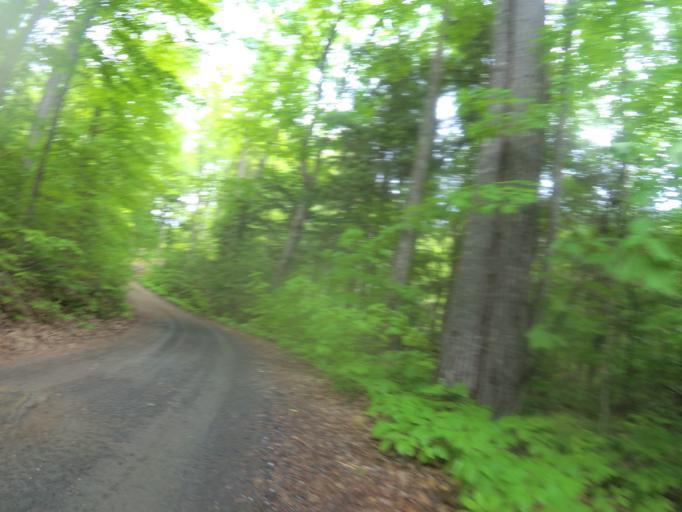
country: CA
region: Ontario
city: Renfrew
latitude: 45.1167
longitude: -76.8216
